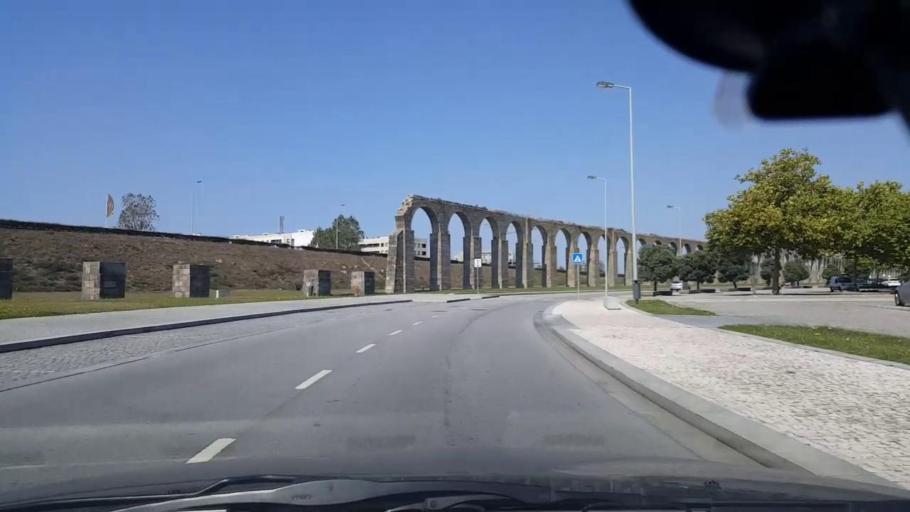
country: PT
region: Porto
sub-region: Vila do Conde
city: Vila do Conde
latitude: 41.3622
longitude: -8.7418
